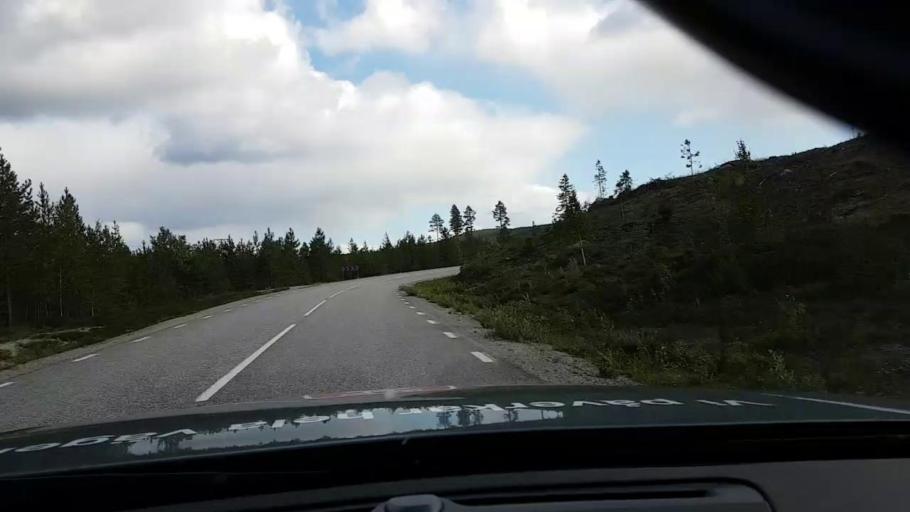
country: SE
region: Vaesternorrland
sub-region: OErnskoeldsviks Kommun
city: Bredbyn
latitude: 63.6788
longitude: 17.7896
